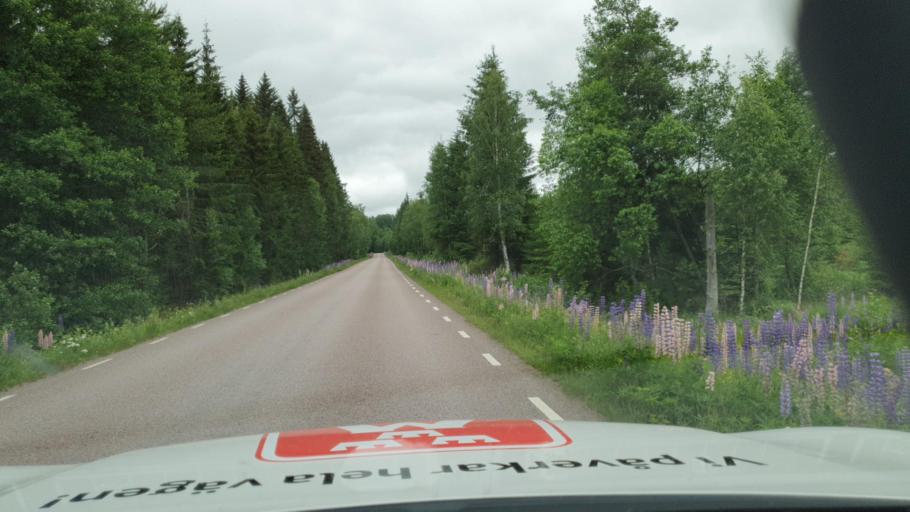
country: SE
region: Vaermland
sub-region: Karlstads Kommun
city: Edsvalla
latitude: 59.4649
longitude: 13.0835
